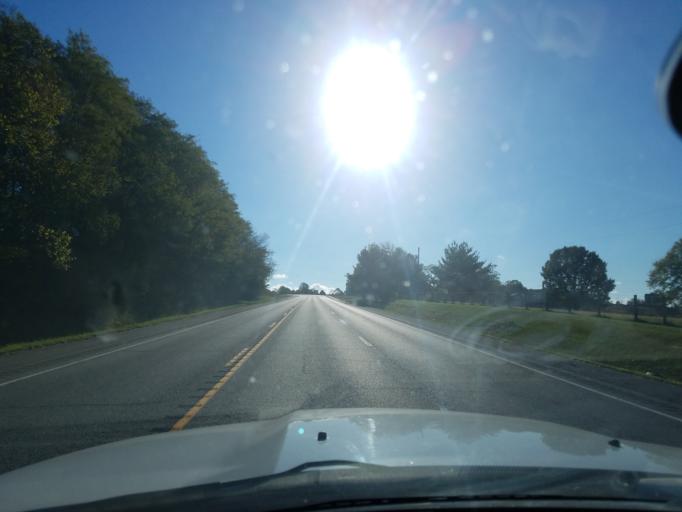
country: US
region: Kentucky
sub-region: Washington County
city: Springfield
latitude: 37.7131
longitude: -85.2671
